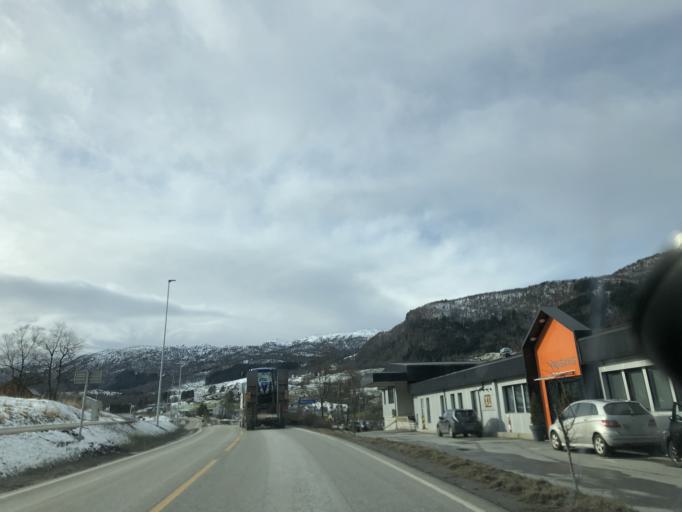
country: NO
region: Rogaland
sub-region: Vindafjord
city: Olen
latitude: 59.5997
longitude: 5.7539
